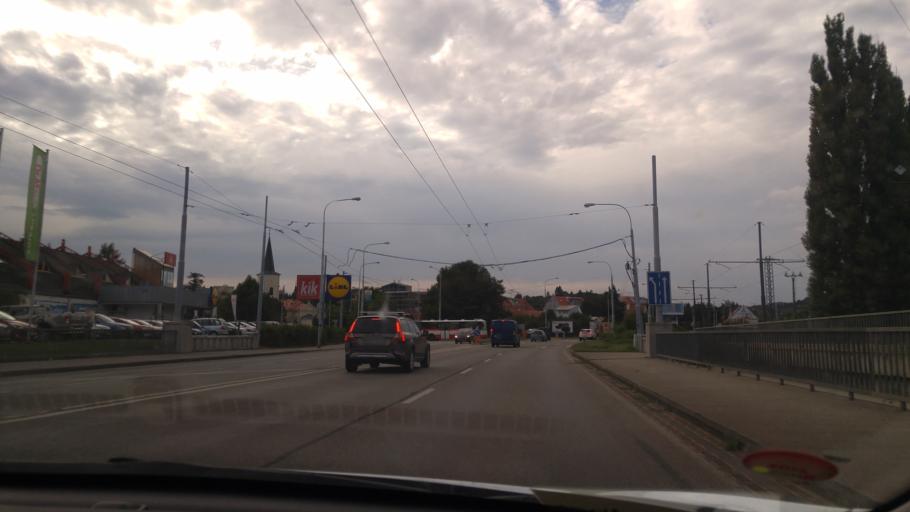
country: CZ
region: South Moravian
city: Troubsko
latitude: 49.2261
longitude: 16.5342
